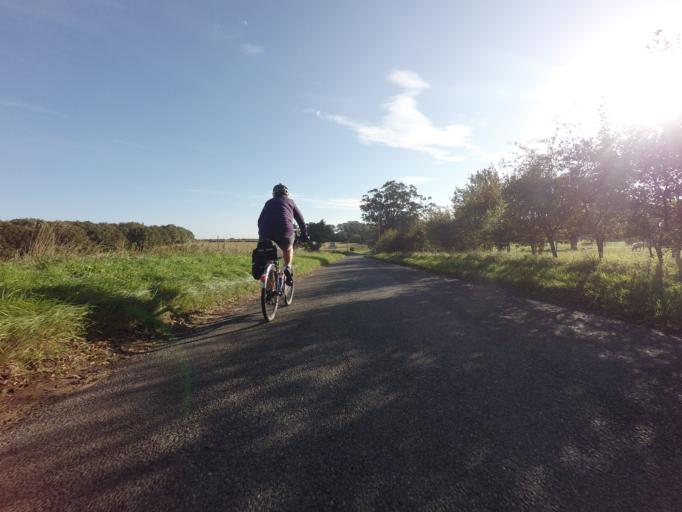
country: GB
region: England
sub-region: Norfolk
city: Dersingham
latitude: 52.8364
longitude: 0.5765
